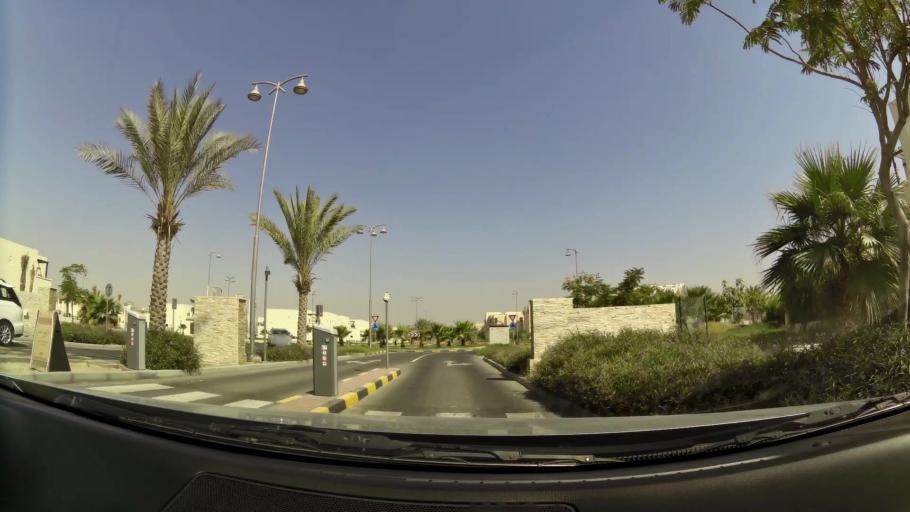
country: AE
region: Dubai
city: Dubai
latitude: 25.0274
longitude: 55.1519
